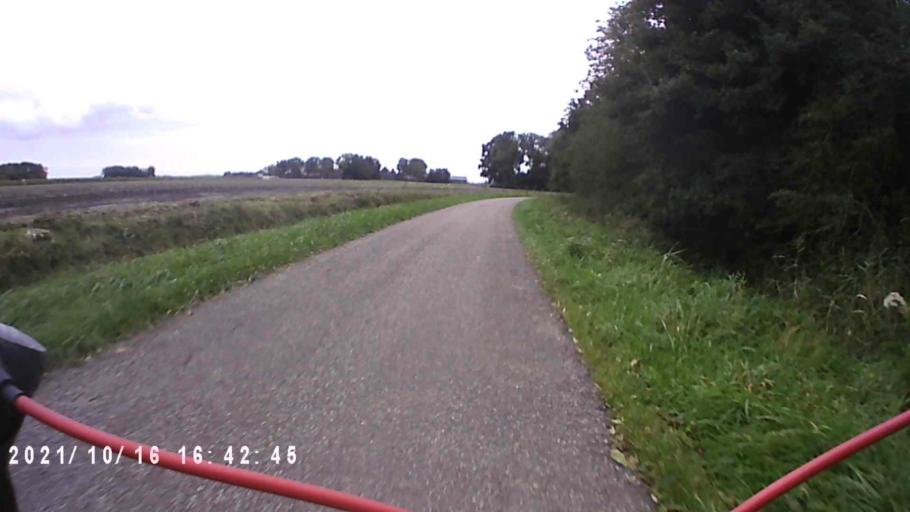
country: NL
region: Friesland
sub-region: Gemeente Dongeradeel
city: Anjum
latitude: 53.3729
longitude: 6.1437
